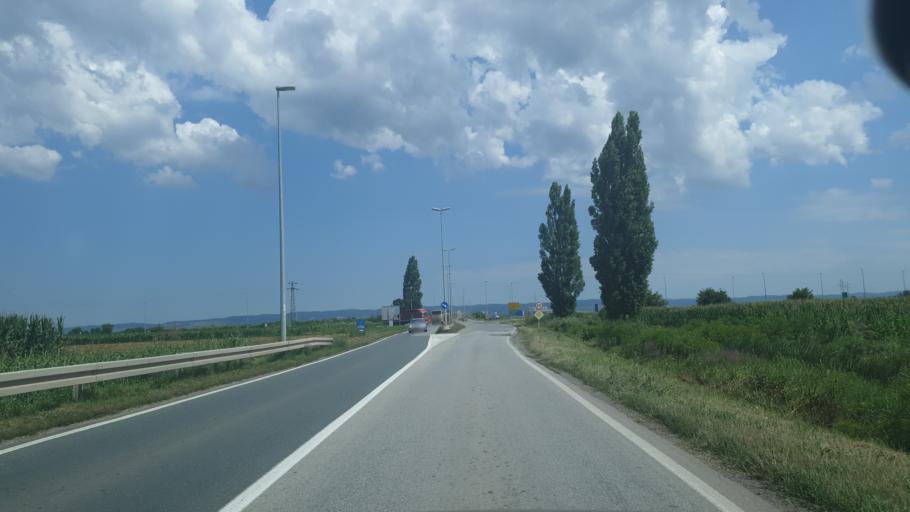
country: RS
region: Autonomna Pokrajina Vojvodina
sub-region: Sremski Okrug
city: Sremska Mitrovica
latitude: 44.9935
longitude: 19.6412
